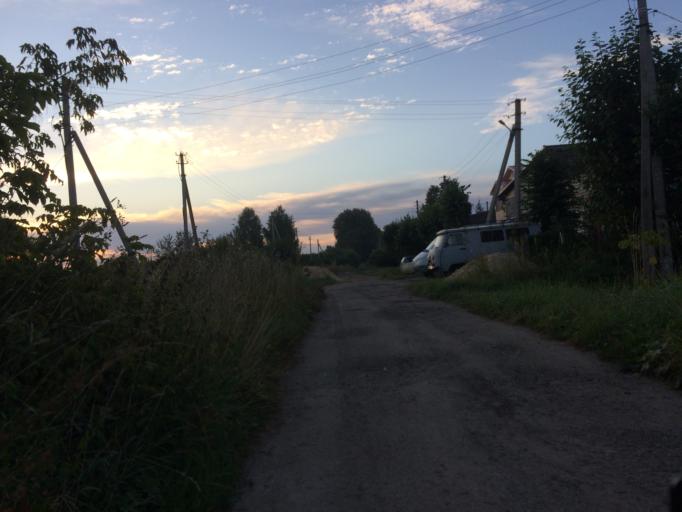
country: RU
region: Mariy-El
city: Yoshkar-Ola
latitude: 56.6550
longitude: 47.9059
